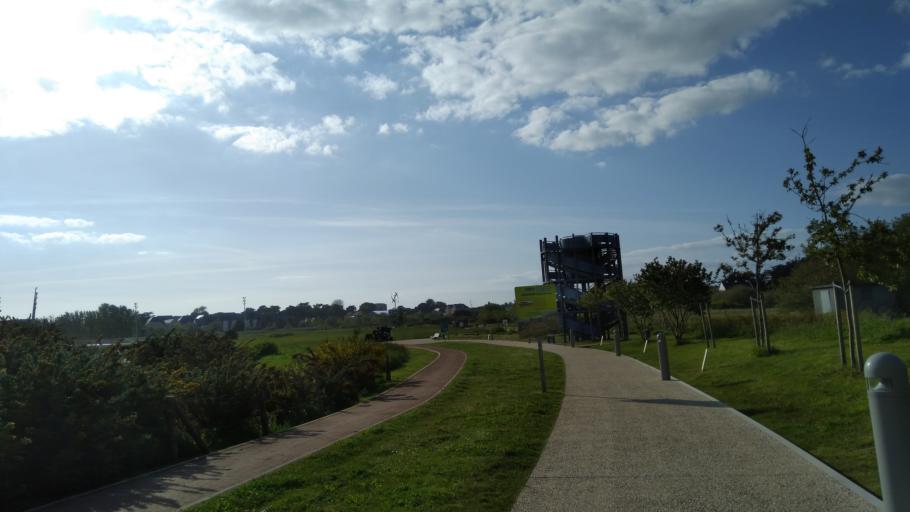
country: FR
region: Pays de la Loire
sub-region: Departement de la Loire-Atlantique
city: Pornichet
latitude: 47.2625
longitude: -2.3274
